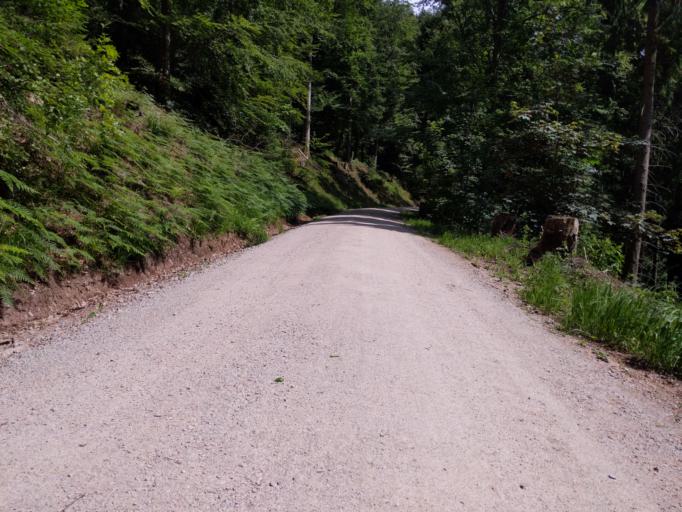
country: DE
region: Baden-Wuerttemberg
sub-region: Karlsruhe Region
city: Bad Rippoldsau-Schapbach
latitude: 48.4130
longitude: 8.3643
